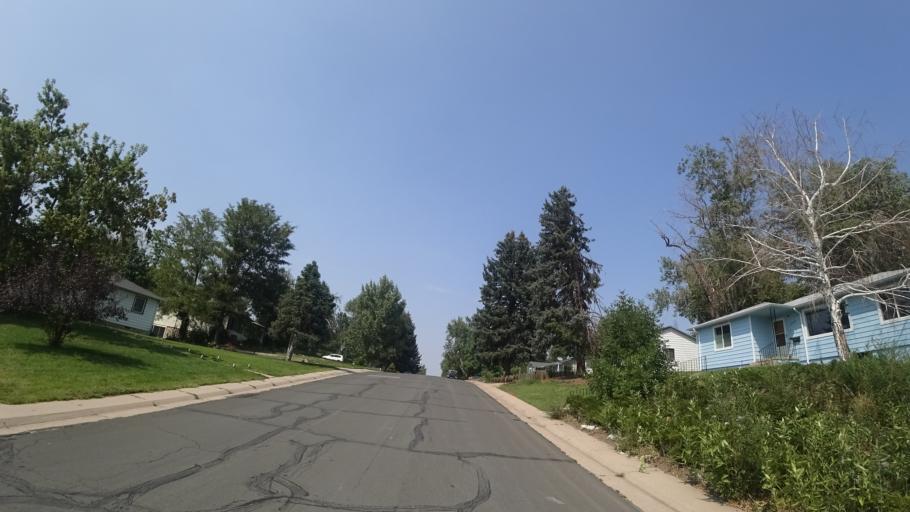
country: US
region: Colorado
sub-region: Arapahoe County
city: Englewood
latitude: 39.6295
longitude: -104.9996
